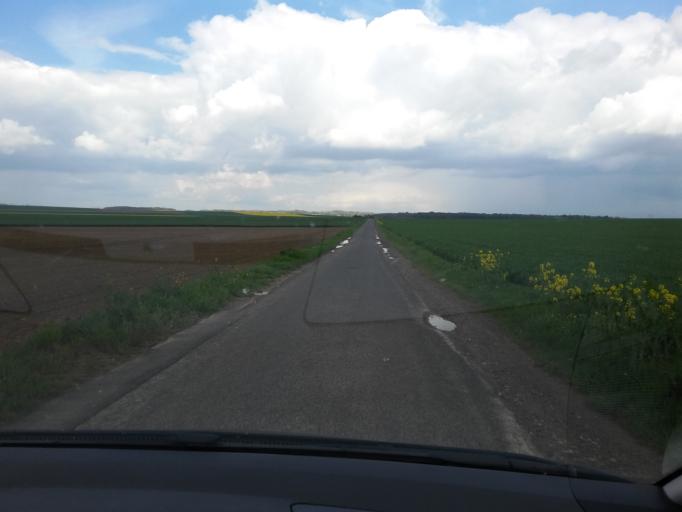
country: FR
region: Picardie
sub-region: Departement de l'Oise
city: Chevrieres
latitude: 49.3596
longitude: 2.6844
